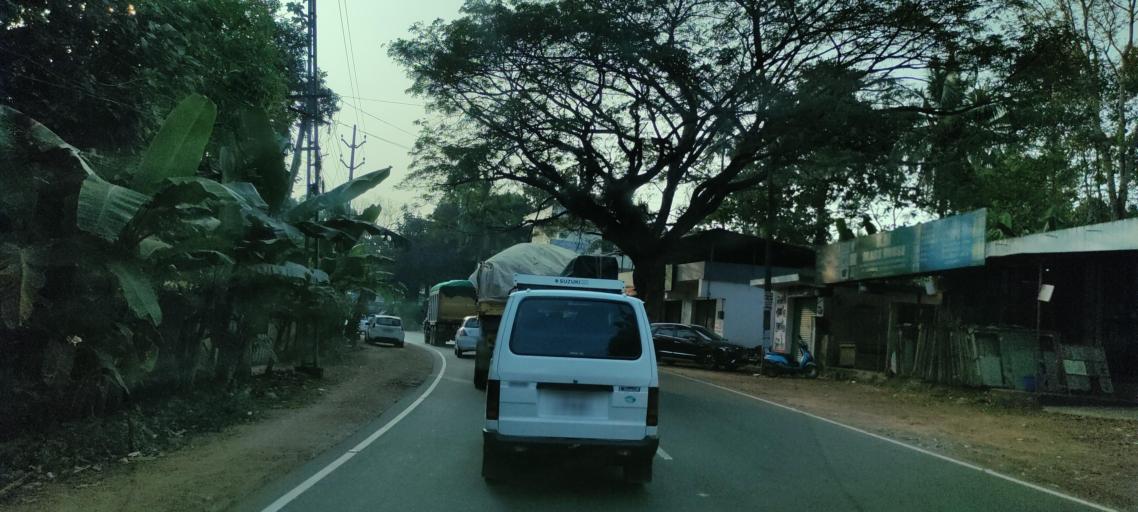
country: IN
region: Kerala
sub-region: Alappuzha
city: Kattanam
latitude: 9.1757
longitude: 76.6154
